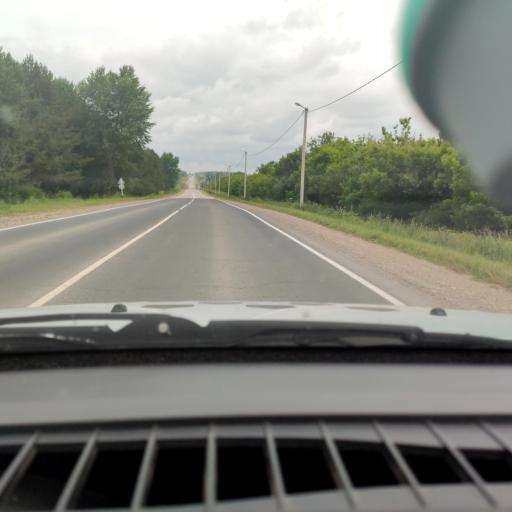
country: RU
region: Perm
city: Ust'-Kishert'
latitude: 57.5967
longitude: 57.3265
